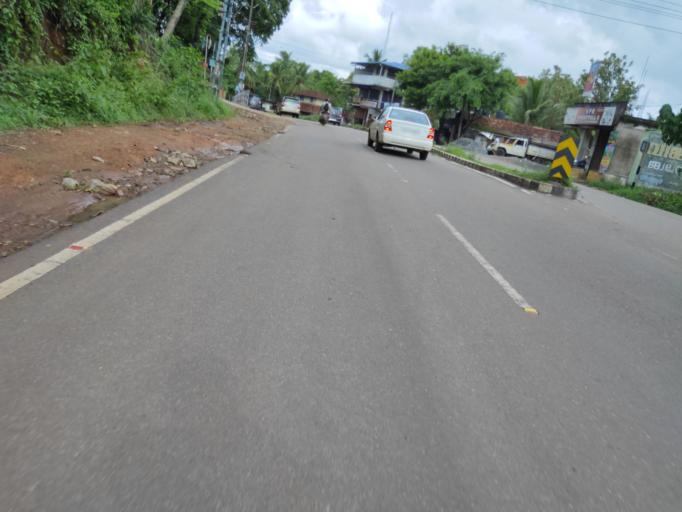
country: IN
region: Kerala
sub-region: Malappuram
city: Manjeri
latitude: 11.1968
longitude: 76.2268
